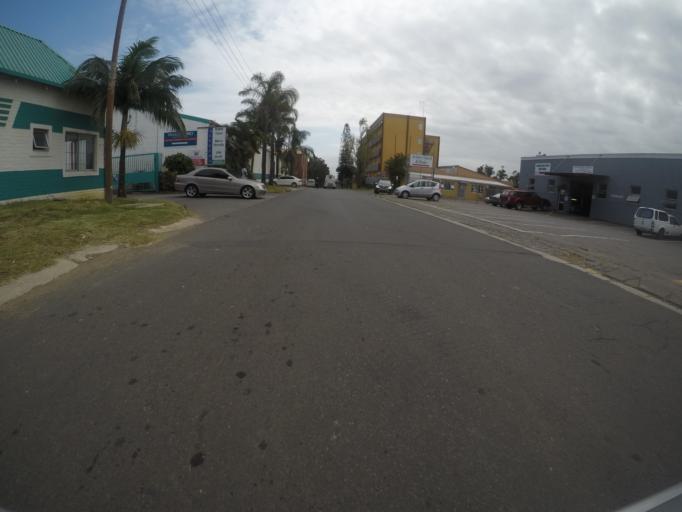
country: ZA
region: Eastern Cape
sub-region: Buffalo City Metropolitan Municipality
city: East London
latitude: -32.9875
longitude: 27.8888
